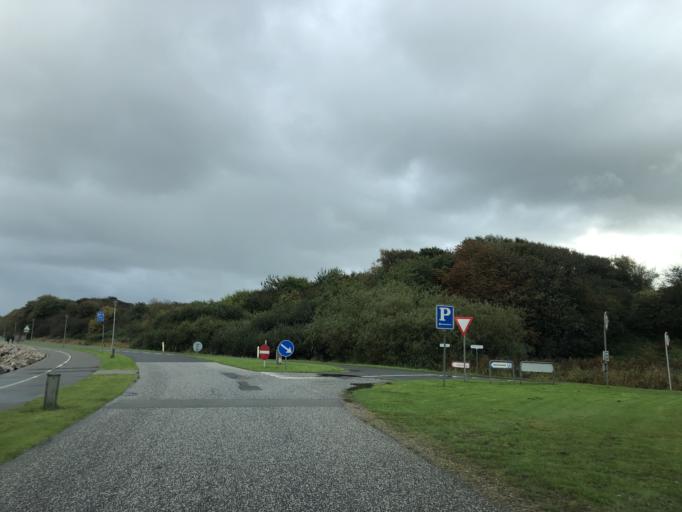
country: DK
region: Central Jutland
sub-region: Lemvig Kommune
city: Lemvig
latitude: 56.5621
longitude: 8.2941
